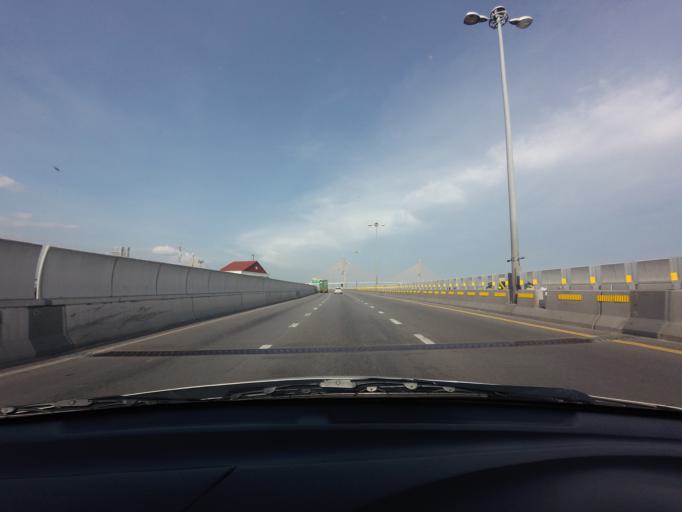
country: TH
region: Samut Prakan
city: Phra Pradaeng
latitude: 13.6640
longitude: 100.5279
